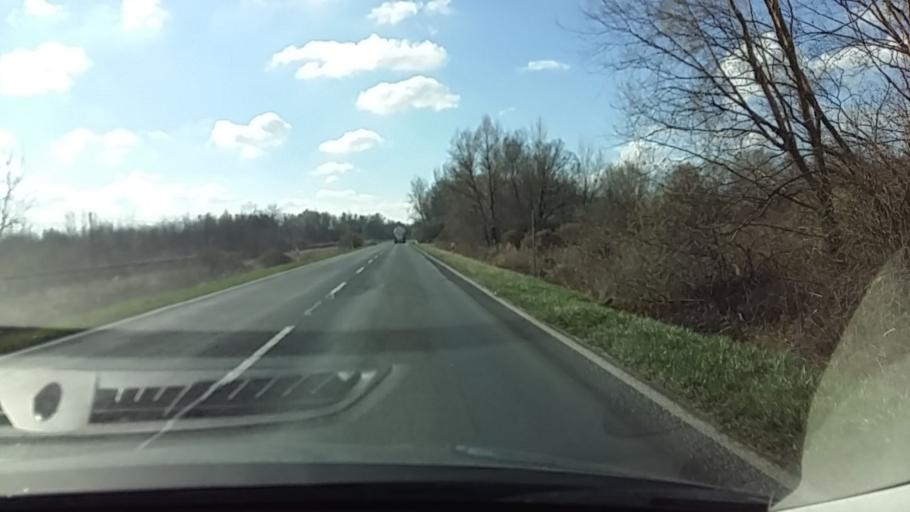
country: HU
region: Veszprem
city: Tapolca
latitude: 46.8165
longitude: 17.3823
